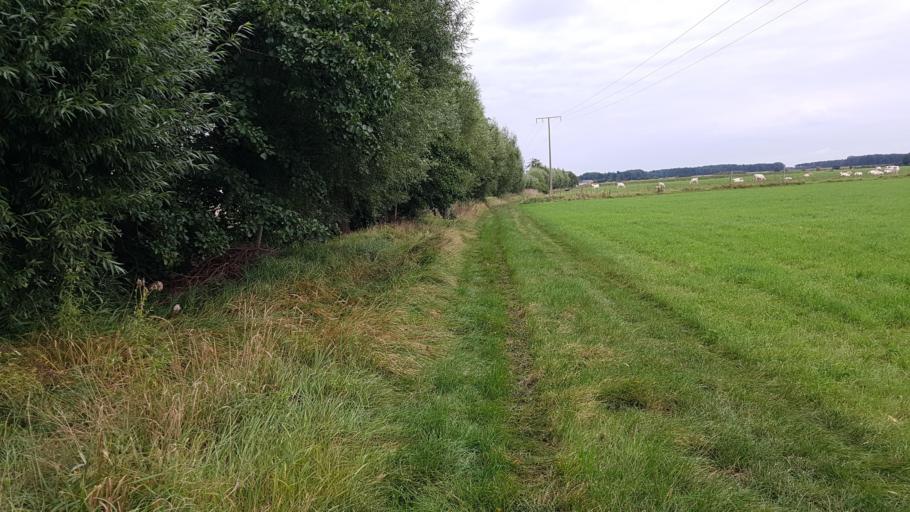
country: DE
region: Brandenburg
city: Doberlug-Kirchhain
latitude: 51.6130
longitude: 13.5725
